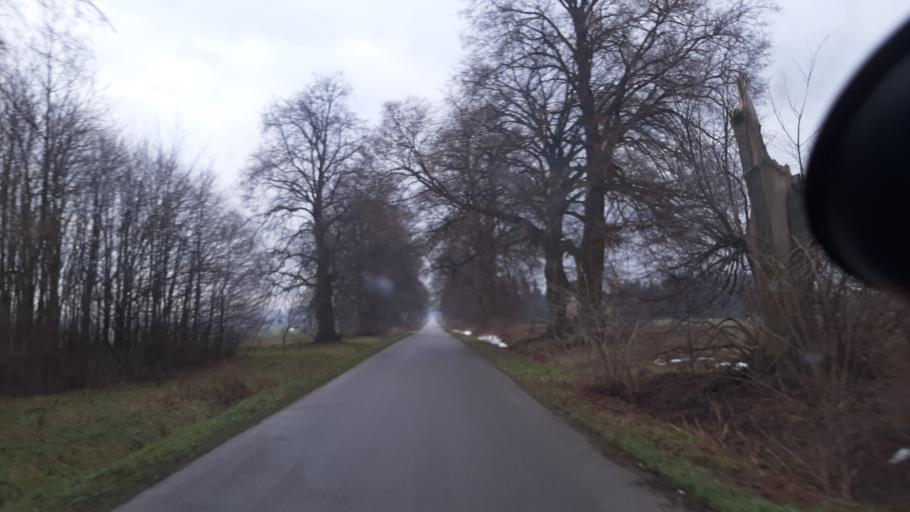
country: PL
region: Lublin Voivodeship
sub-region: Powiat lubelski
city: Lublin
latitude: 51.3407
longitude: 22.5357
